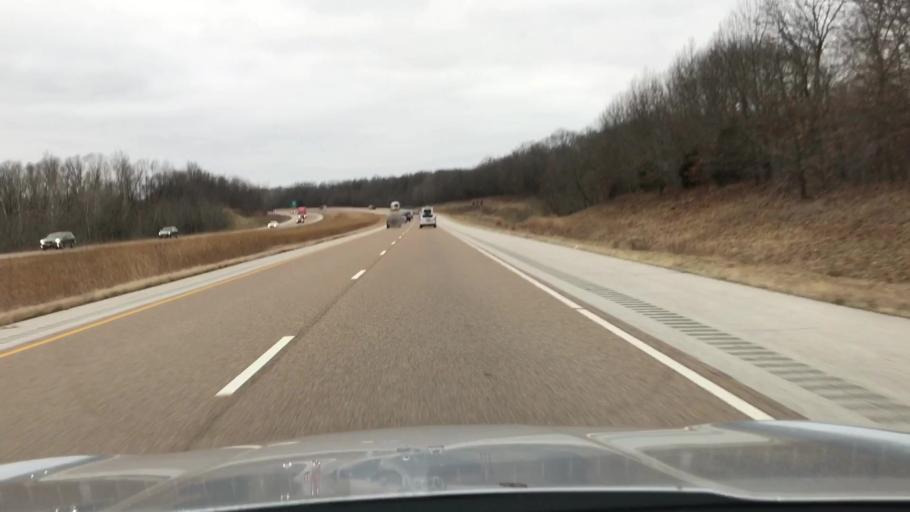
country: US
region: Illinois
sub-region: Macoupin County
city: Mount Olive
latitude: 39.0870
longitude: -89.7496
